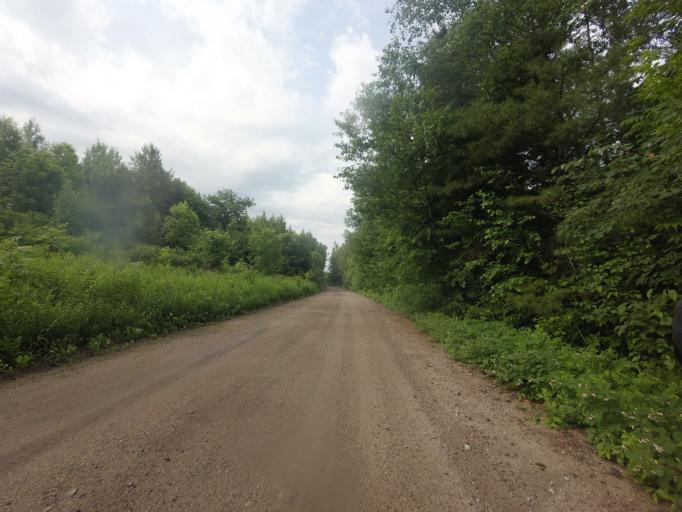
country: CA
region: Quebec
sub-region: Outaouais
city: Maniwaki
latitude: 46.3227
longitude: -76.0058
